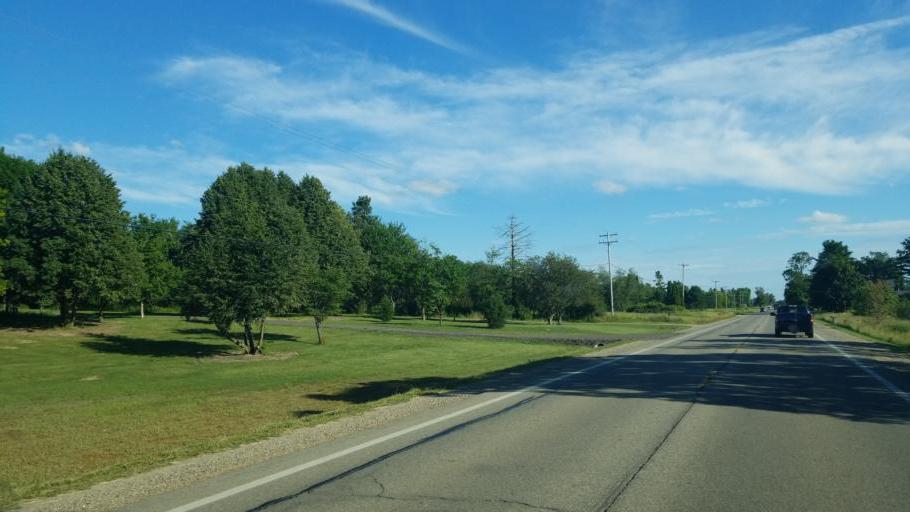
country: US
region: Michigan
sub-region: Eaton County
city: Charlotte
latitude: 42.5286
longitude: -84.8359
